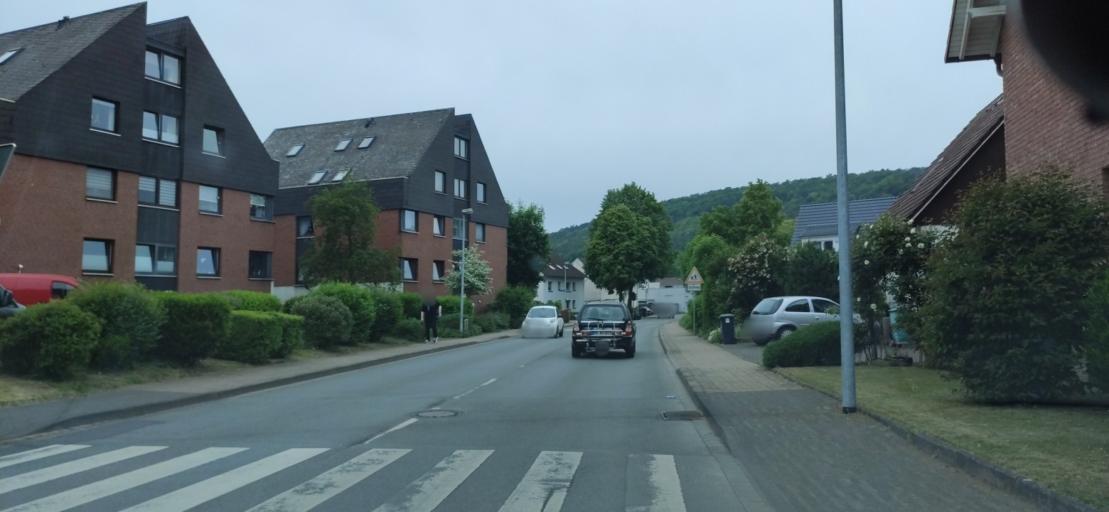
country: DE
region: North Rhine-Westphalia
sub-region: Regierungsbezirk Detmold
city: Hoexter
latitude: 51.7716
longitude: 9.3724
